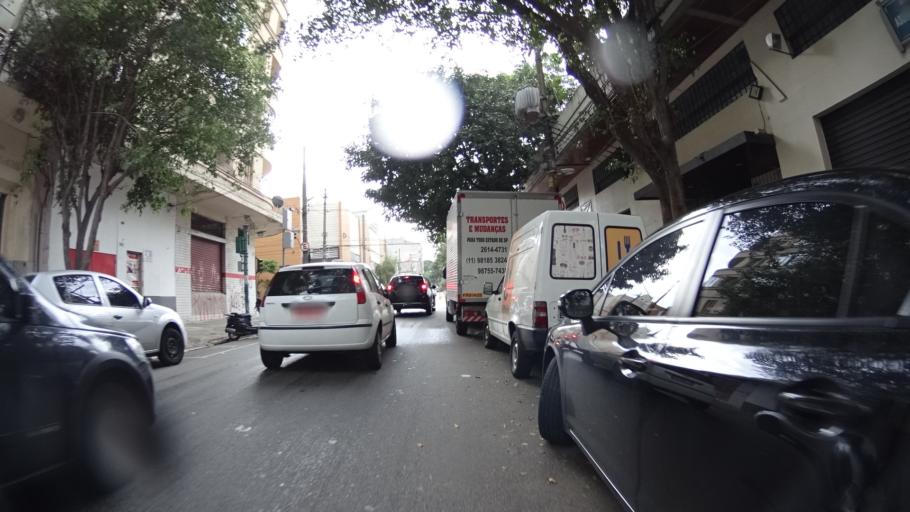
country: BR
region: Sao Paulo
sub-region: Sao Paulo
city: Sao Paulo
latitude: -23.5358
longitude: -46.6506
